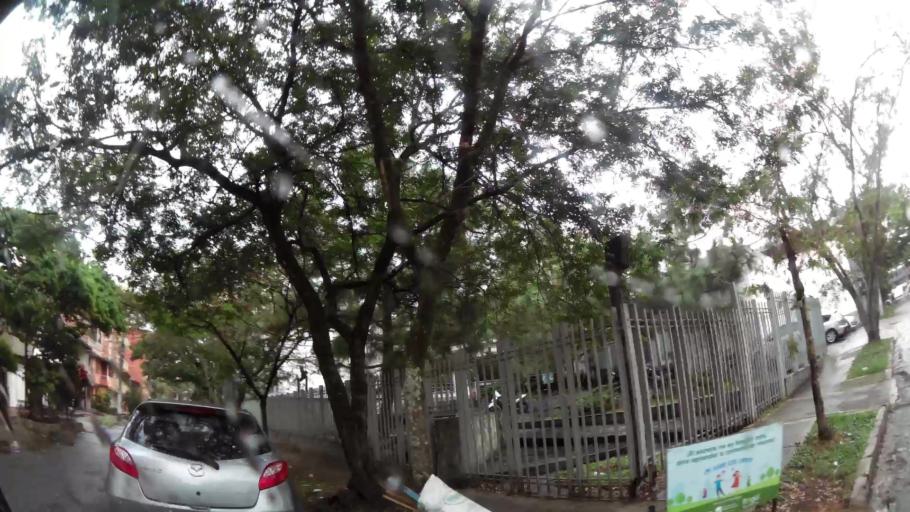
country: CO
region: Antioquia
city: Itagui
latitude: 6.1850
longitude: -75.5982
